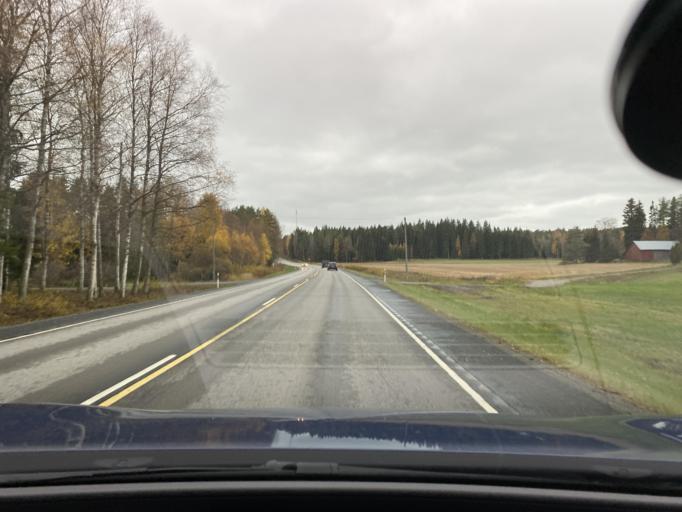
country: FI
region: Satakunta
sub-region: Rauma
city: Lappi
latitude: 61.1183
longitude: 21.9336
